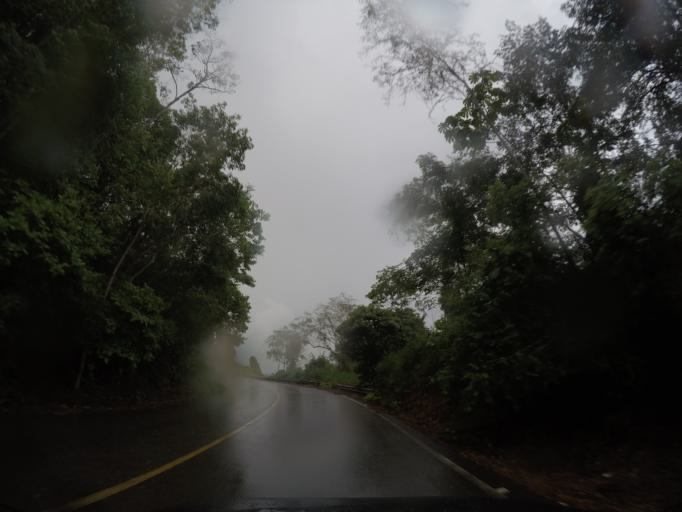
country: MX
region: Oaxaca
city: San Gabriel Mixtepec
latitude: 16.0812
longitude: -97.0813
